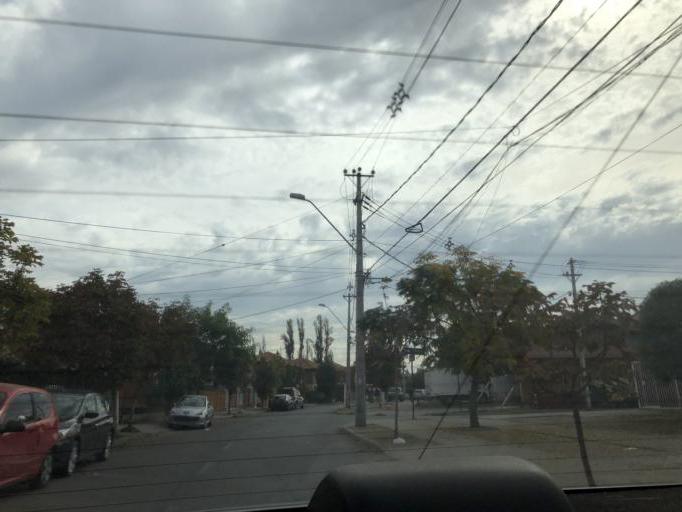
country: CL
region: Santiago Metropolitan
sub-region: Provincia de Cordillera
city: Puente Alto
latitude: -33.6116
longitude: -70.5247
